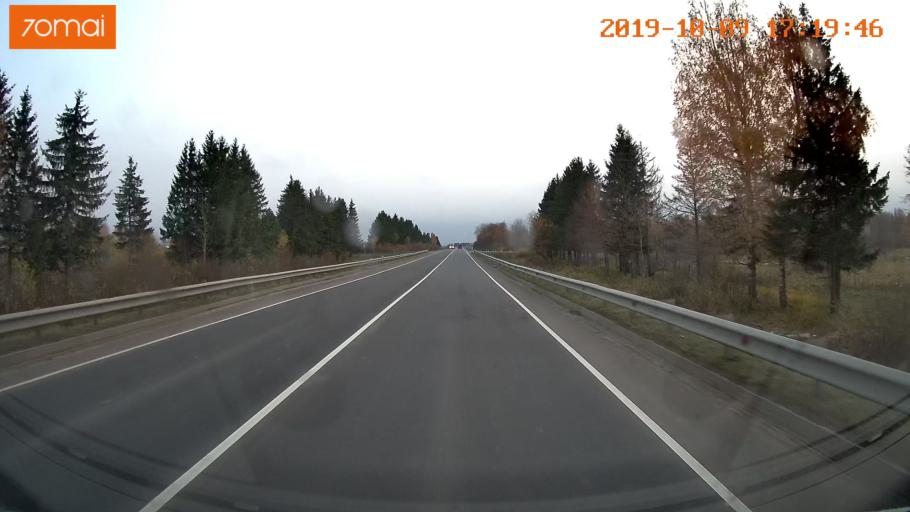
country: RU
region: Ivanovo
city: Furmanov
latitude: 57.2421
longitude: 41.1489
